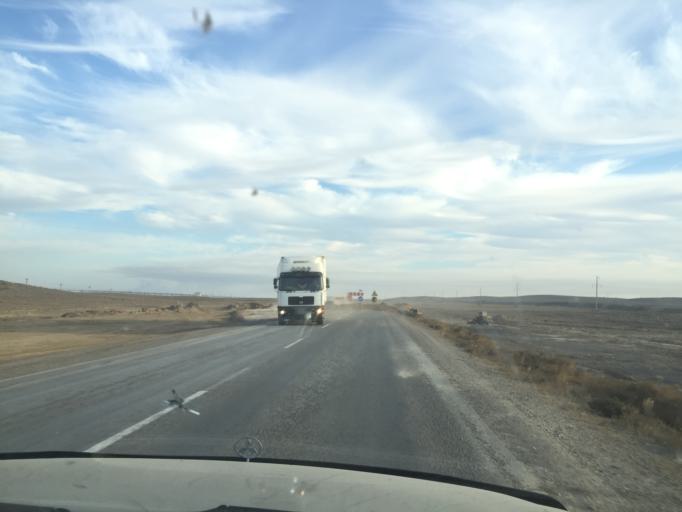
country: KZ
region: Almaty Oblysy
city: Ulken
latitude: 45.1838
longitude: 73.9216
